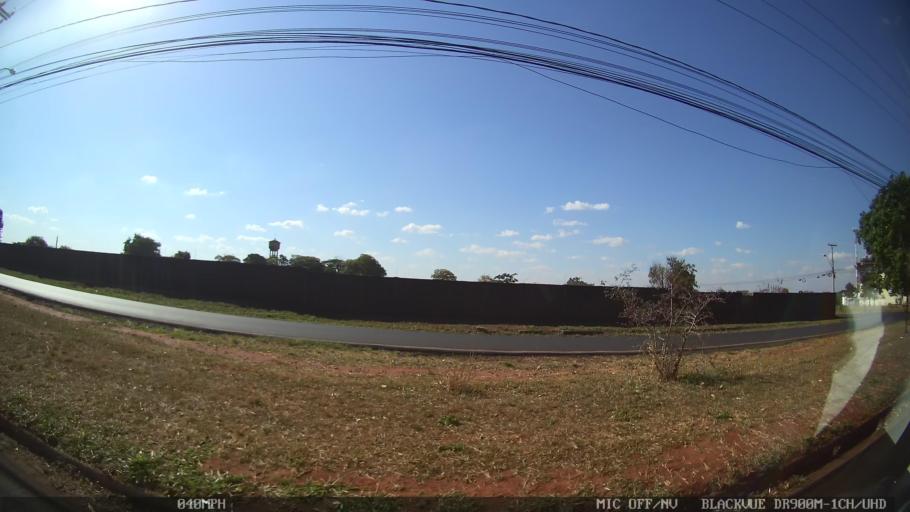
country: BR
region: Sao Paulo
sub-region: Ribeirao Preto
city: Ribeirao Preto
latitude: -21.1518
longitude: -47.7624
